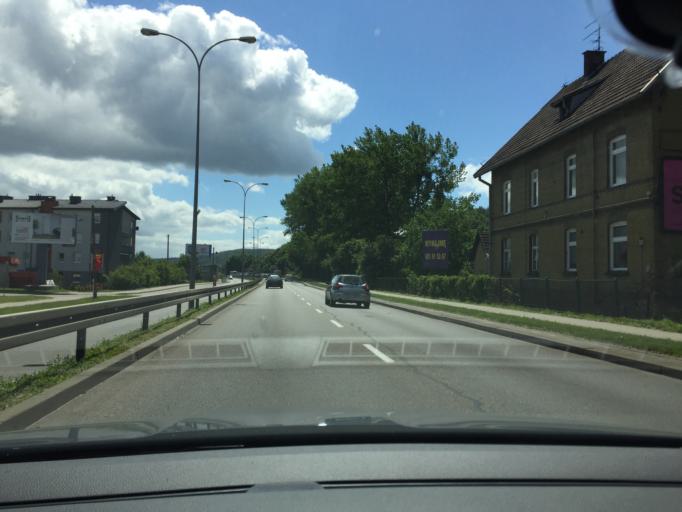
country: PL
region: Pomeranian Voivodeship
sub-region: Powiat wejherowski
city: Reda
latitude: 54.5934
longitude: 18.3556
